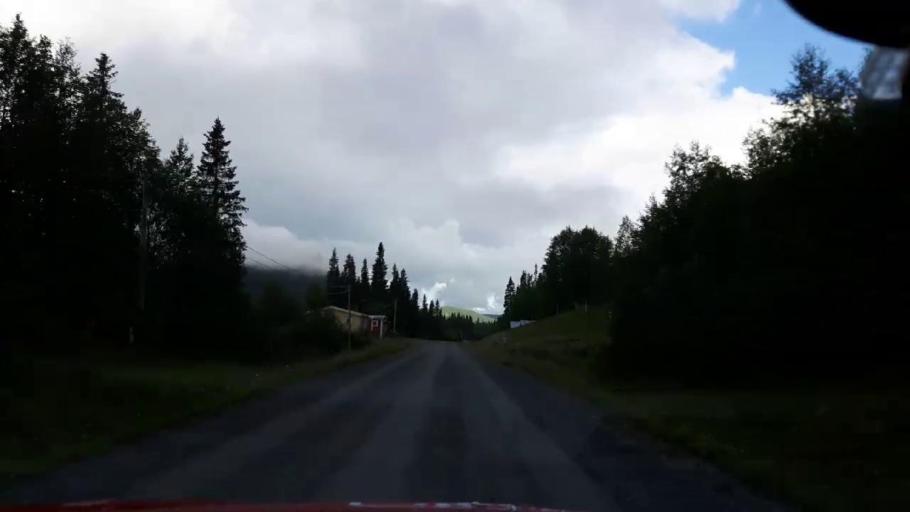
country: NO
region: Nordland
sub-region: Hattfjelldal
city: Hattfjelldal
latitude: 64.8822
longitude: 14.7885
